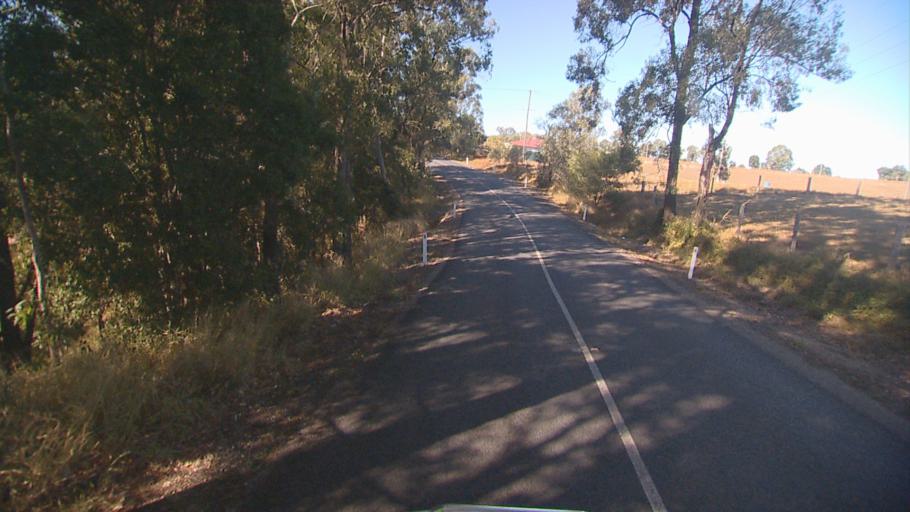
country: AU
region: Queensland
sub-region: Logan
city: Cedar Vale
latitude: -27.8978
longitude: 153.0154
